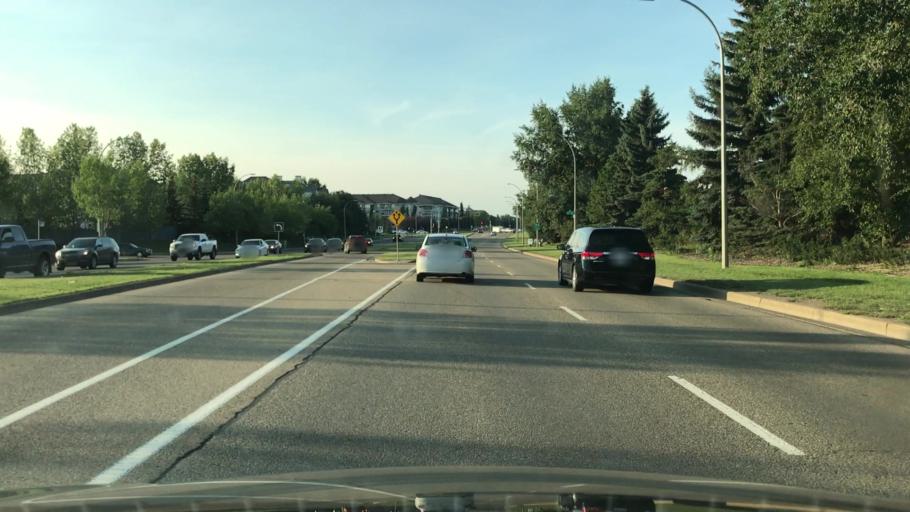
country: CA
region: Alberta
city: Beaumont
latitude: 53.4560
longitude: -113.4203
